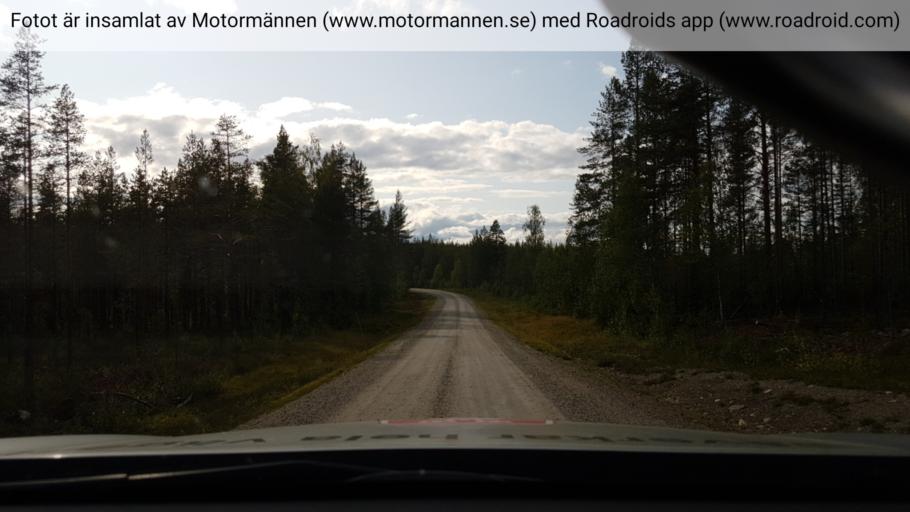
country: SE
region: Vaesterbotten
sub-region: Lycksele Kommun
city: Lycksele
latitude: 64.7276
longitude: 19.0246
